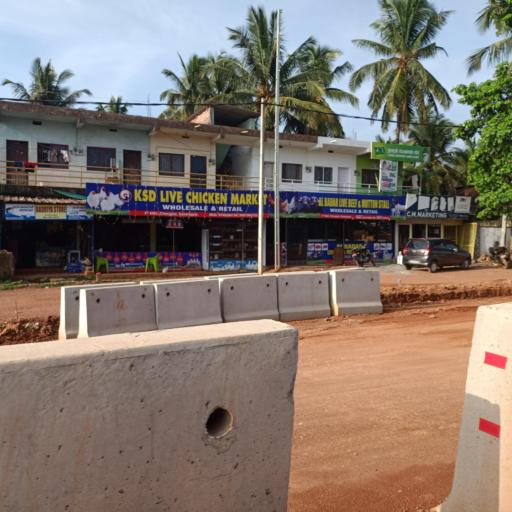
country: IN
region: Kerala
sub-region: Kasaragod District
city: Kasaragod
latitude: 12.5111
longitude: 75.0335
